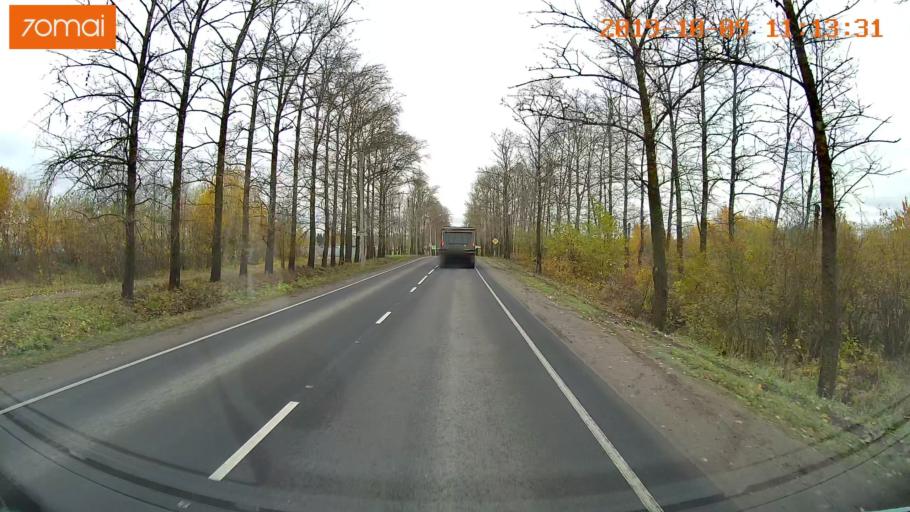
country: RU
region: Vologda
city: Vologda
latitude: 59.1824
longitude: 39.8441
